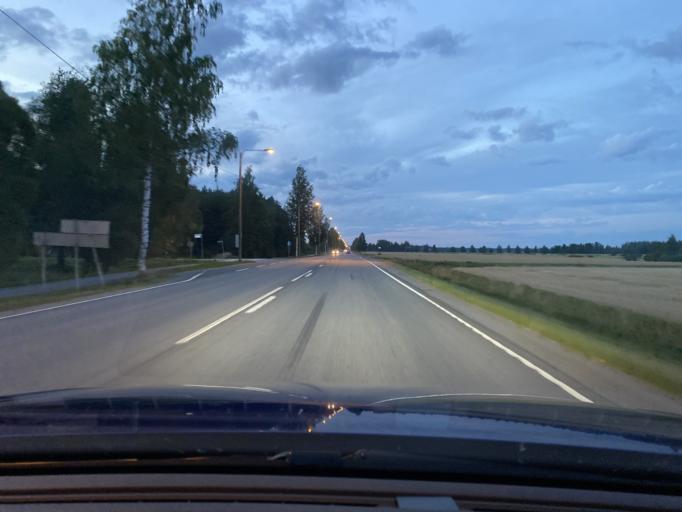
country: FI
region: Southern Ostrobothnia
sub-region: Suupohja
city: Kauhajoki
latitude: 62.4321
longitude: 22.2049
